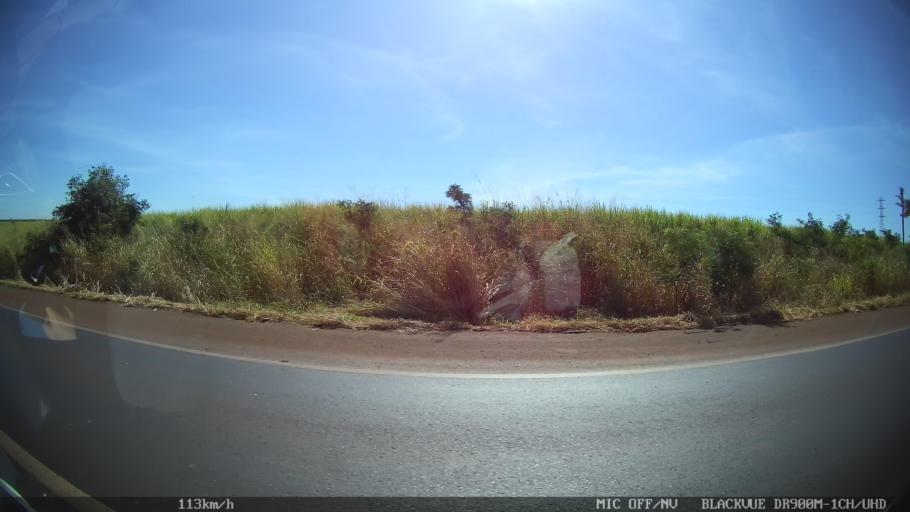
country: BR
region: Sao Paulo
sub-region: Barretos
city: Barretos
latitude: -20.5032
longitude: -48.5455
